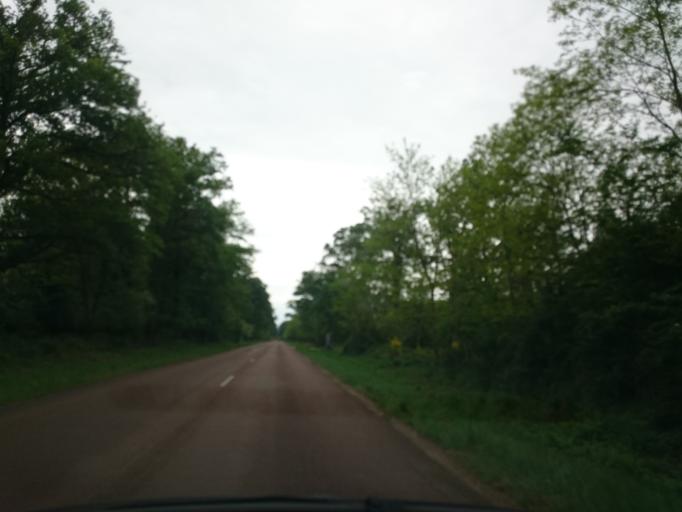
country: FR
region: Centre
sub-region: Departement du Loir-et-Cher
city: Muides-sur-Loire
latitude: 47.6425
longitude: 1.5236
